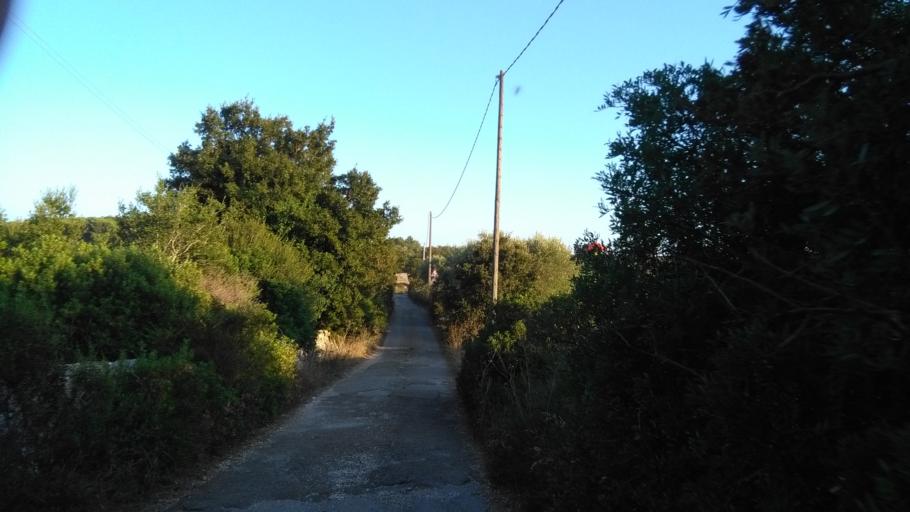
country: IT
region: Apulia
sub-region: Provincia di Bari
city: Putignano
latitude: 40.8275
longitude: 17.0773
